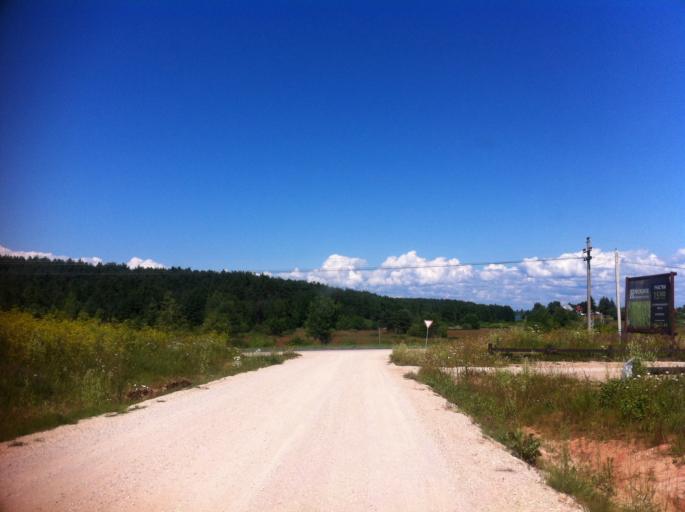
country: RU
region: Pskov
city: Izborsk
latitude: 57.8323
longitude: 27.9645
